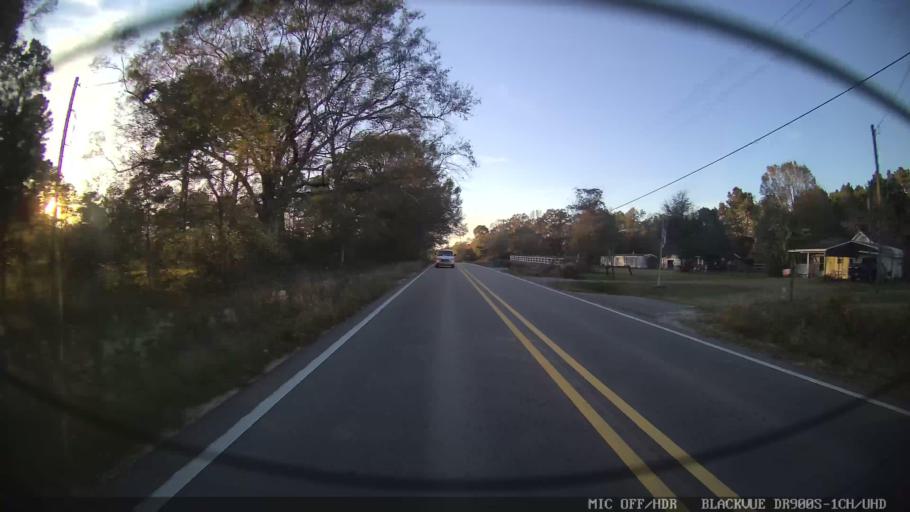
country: US
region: Mississippi
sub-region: Stone County
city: Wiggins
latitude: 30.9878
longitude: -89.2606
